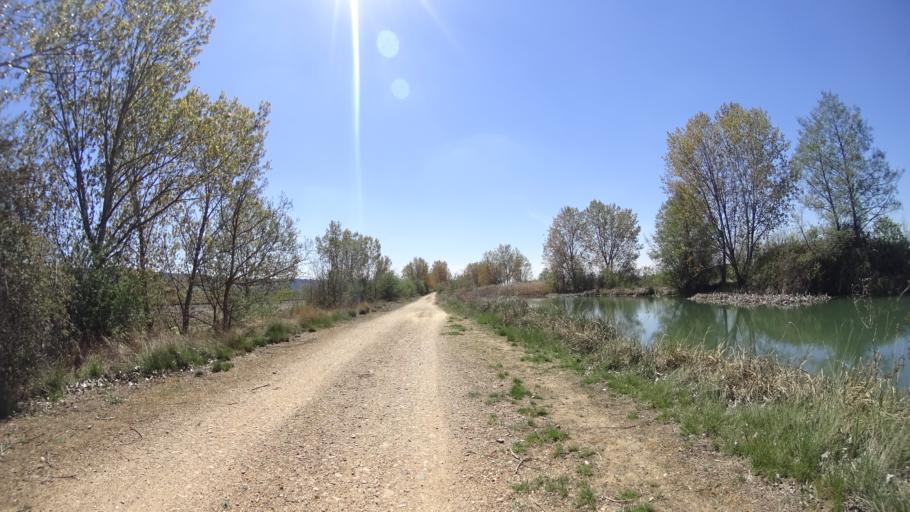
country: ES
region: Castille and Leon
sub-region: Provincia de Valladolid
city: Cabezon
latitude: 41.7740
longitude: -4.6167
